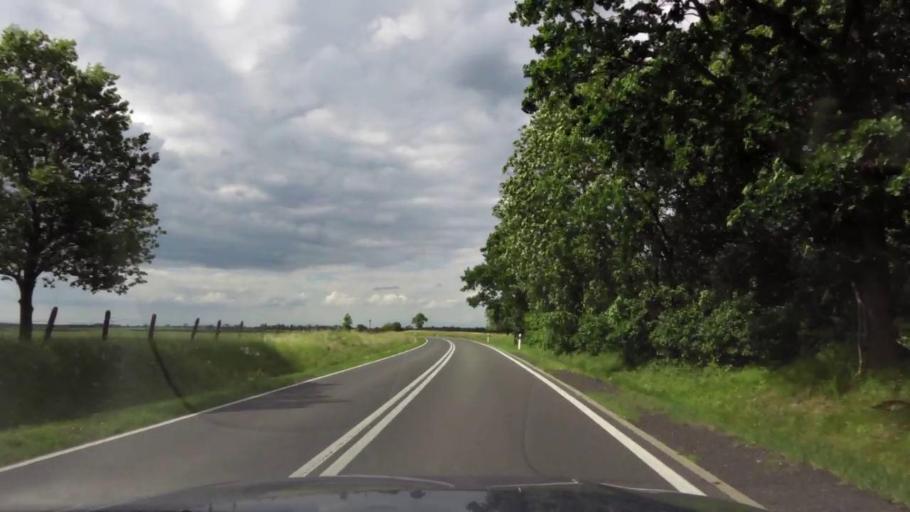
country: PL
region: West Pomeranian Voivodeship
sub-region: Powiat gryfinski
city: Mieszkowice
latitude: 52.8503
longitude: 14.4910
